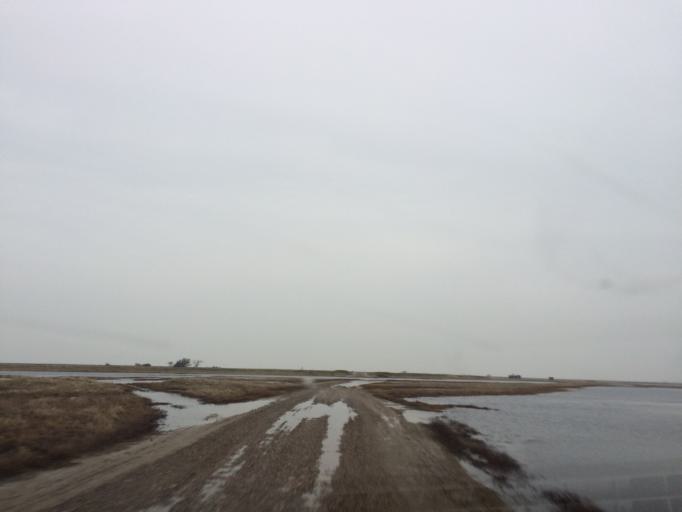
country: DK
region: Central Jutland
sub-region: Lemvig Kommune
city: Lemvig
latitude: 56.5886
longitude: 8.2925
